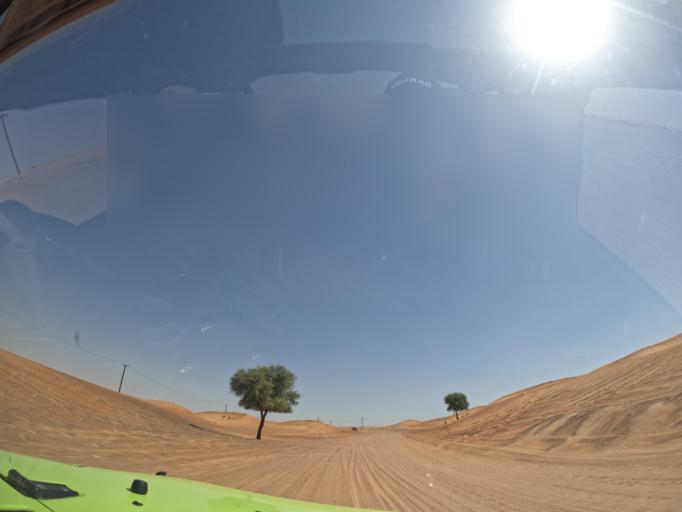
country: AE
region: Ash Shariqah
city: Adh Dhayd
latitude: 25.0167
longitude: 55.7463
